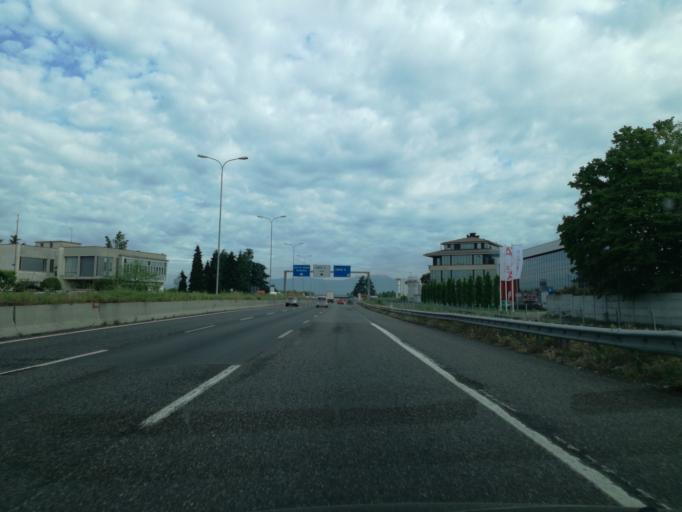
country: IT
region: Lombardy
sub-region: Provincia di Monza e Brianza
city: Carate Brianza
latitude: 45.6571
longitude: 9.2258
